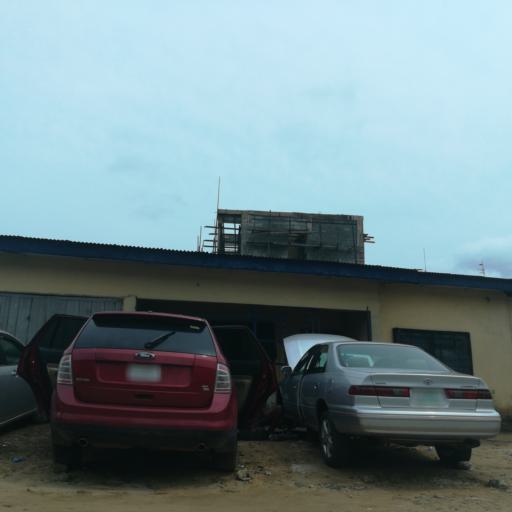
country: NG
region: Rivers
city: Port Harcourt
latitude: 4.8016
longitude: 7.0056
